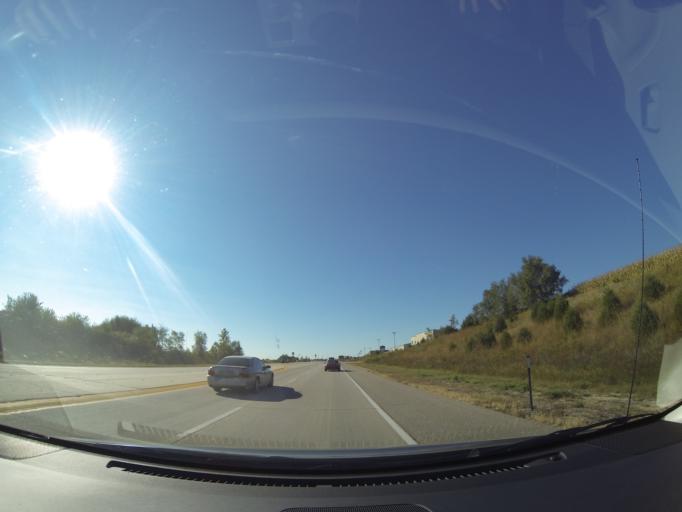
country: US
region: Nebraska
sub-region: Sarpy County
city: Gretna
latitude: 41.1115
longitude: -96.2535
